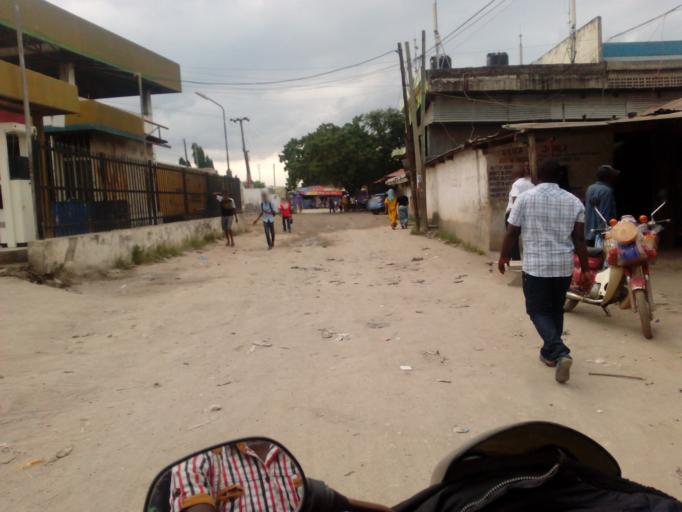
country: TZ
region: Dar es Salaam
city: Dar es Salaam
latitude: -6.8414
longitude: 39.2738
